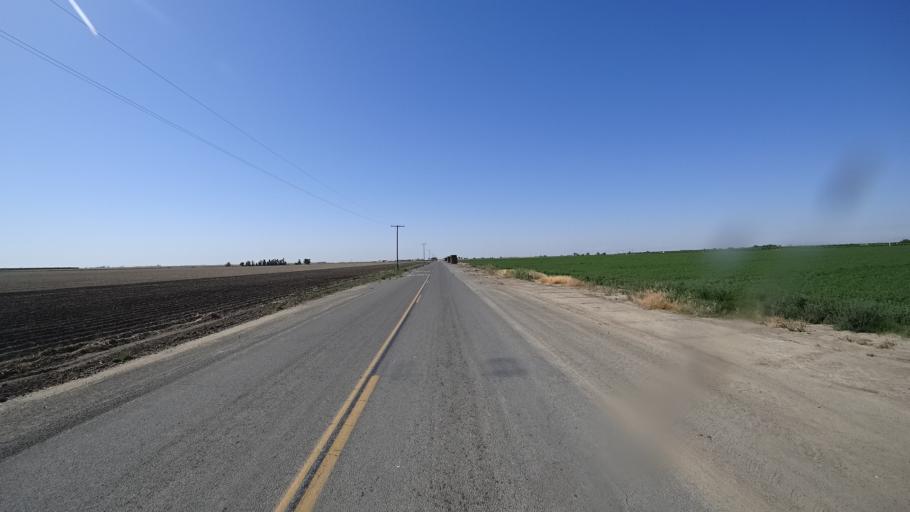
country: US
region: California
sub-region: Kings County
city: Home Garden
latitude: 36.2689
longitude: -119.5475
